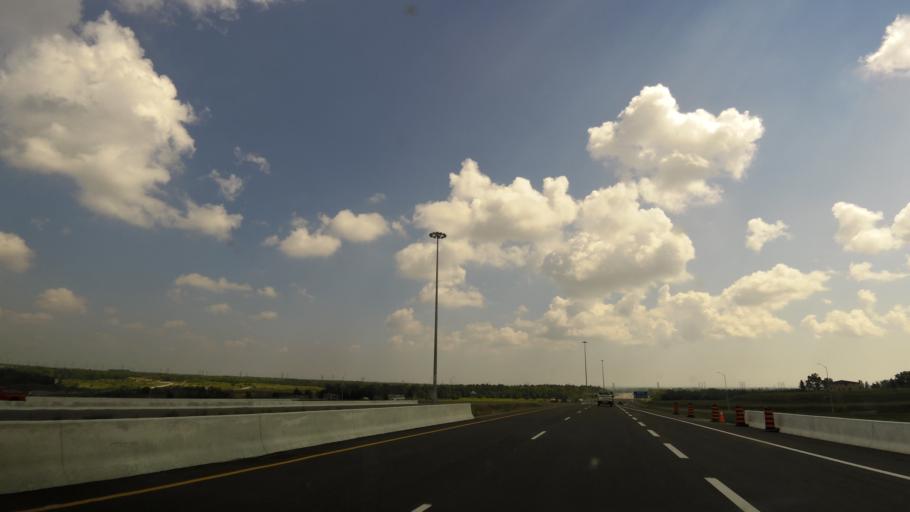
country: CA
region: Ontario
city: Ajax
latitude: 43.9423
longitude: -79.0074
